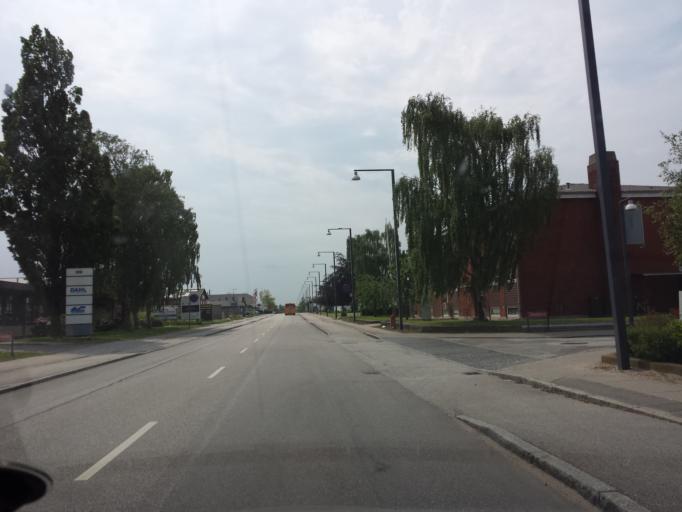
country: DK
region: Capital Region
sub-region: Herlev Kommune
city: Herlev
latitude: 55.7028
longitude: 12.4320
